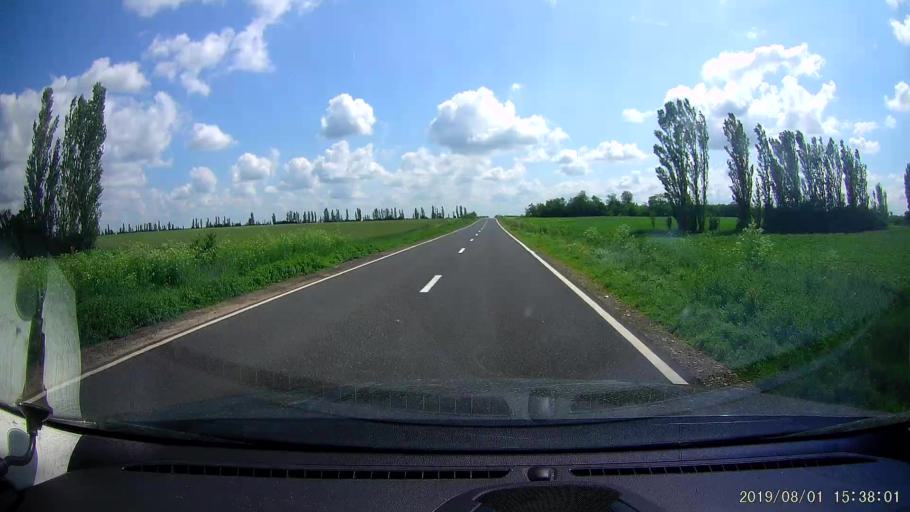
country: RO
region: Braila
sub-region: Comuna Insuratei
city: Insuratei
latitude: 44.8915
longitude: 27.5821
